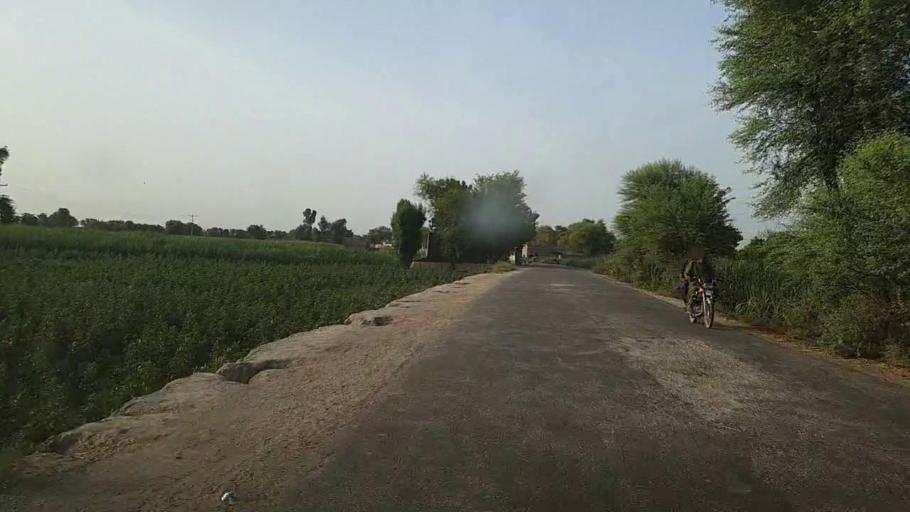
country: PK
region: Sindh
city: Ubauro
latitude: 28.1763
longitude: 69.8292
